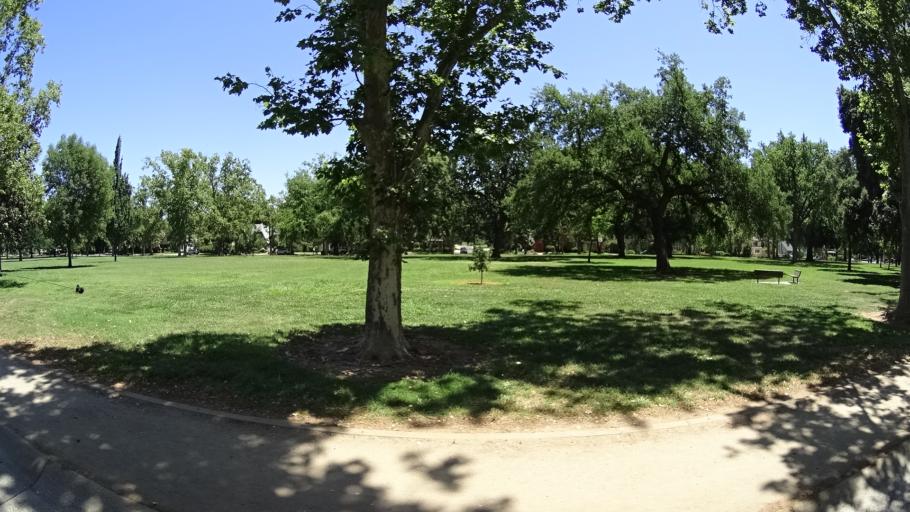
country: US
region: California
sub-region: Sacramento County
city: Sacramento
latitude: 38.5420
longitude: -121.4802
